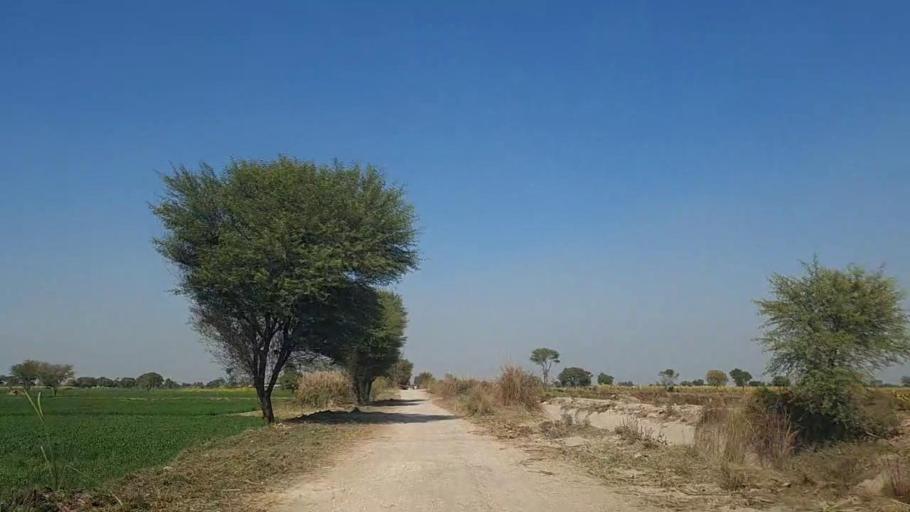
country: PK
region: Sindh
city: Sakrand
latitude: 26.2652
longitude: 68.2209
